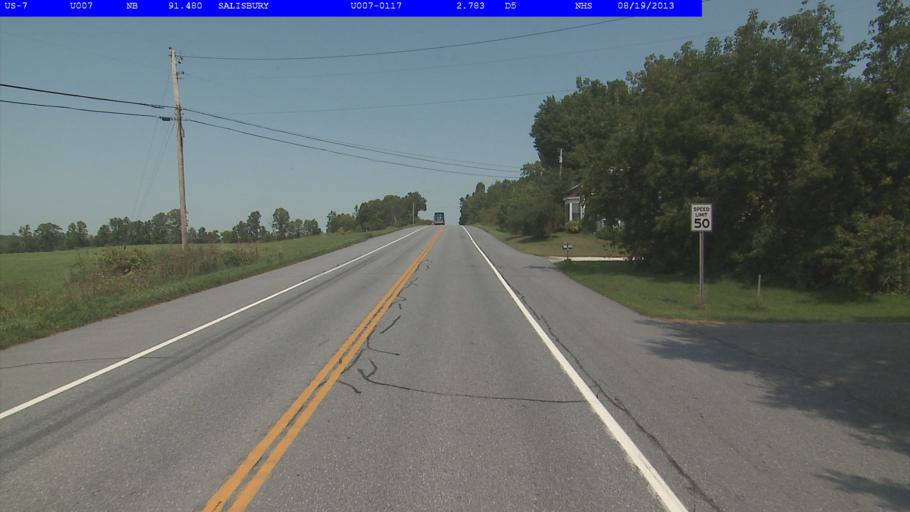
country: US
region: Vermont
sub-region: Addison County
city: Middlebury (village)
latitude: 43.9318
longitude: -73.1089
